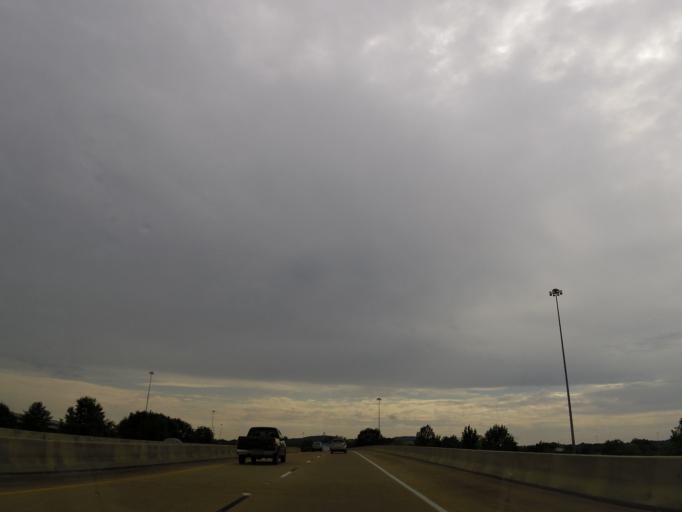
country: US
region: Alabama
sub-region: Madison County
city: Huntsville
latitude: 34.7381
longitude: -86.5896
